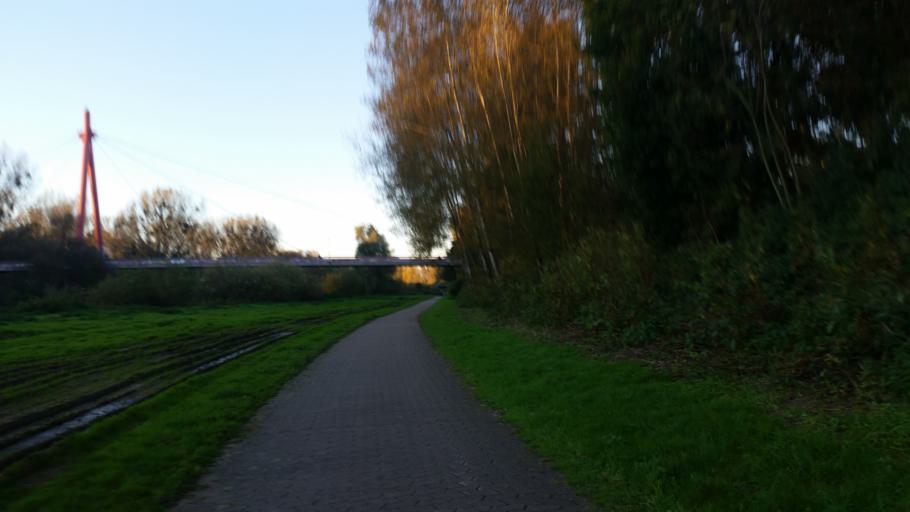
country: DE
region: Lower Saxony
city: Hannover
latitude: 52.3543
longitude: 9.7295
